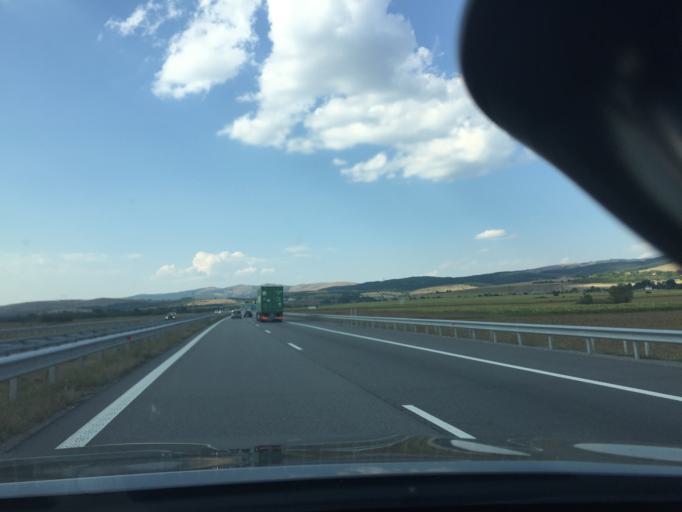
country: BG
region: Kyustendil
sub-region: Obshtina Bobovdol
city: Bobovdol
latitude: 42.4401
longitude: 23.1123
